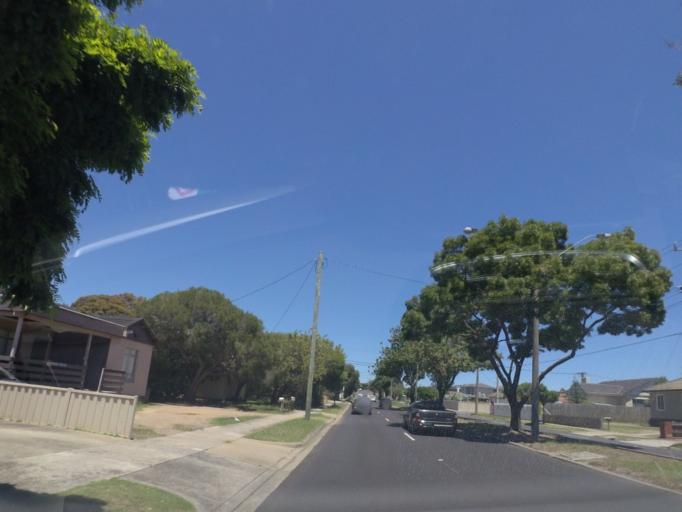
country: AU
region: Victoria
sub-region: Darebin
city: Kingsbury
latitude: -37.7300
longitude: 145.0256
